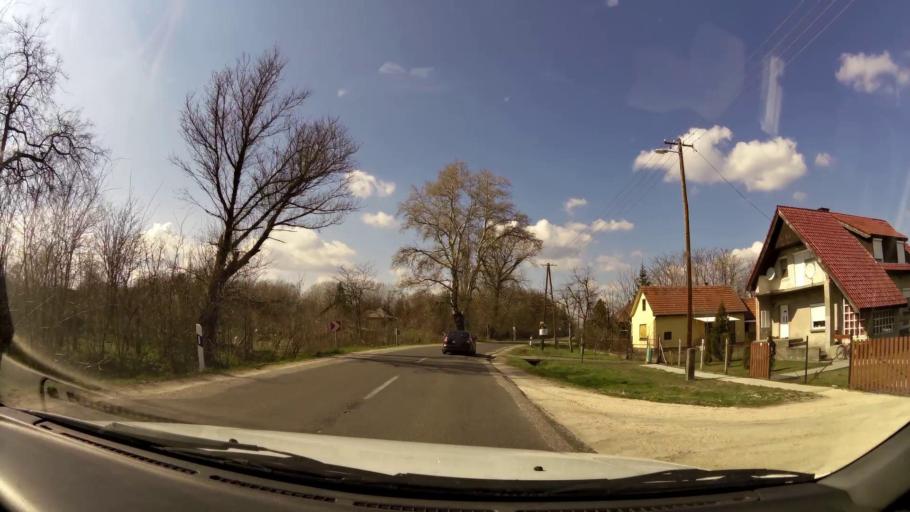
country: HU
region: Pest
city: Farmos
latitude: 47.3682
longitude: 19.7995
